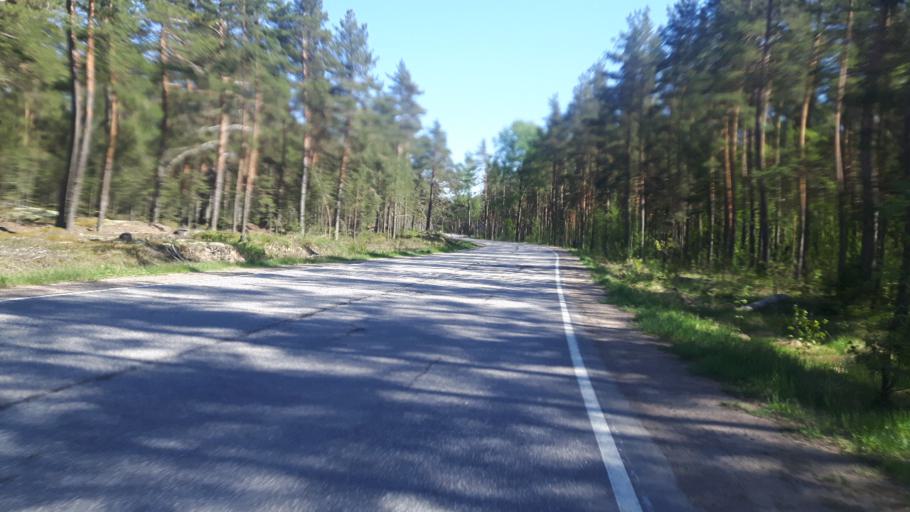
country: RU
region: Leningrad
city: Glebychevo
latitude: 60.2755
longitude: 28.9294
